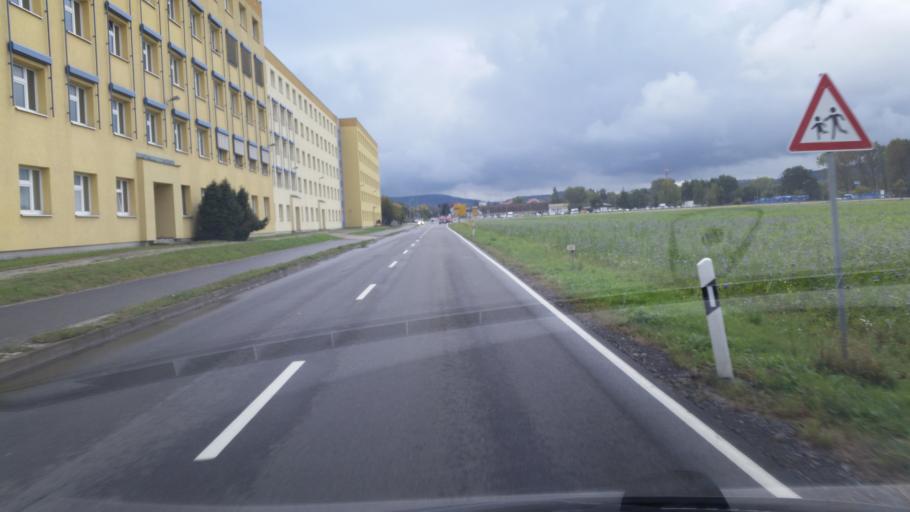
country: DE
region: Saxony
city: Kamenz
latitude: 51.2934
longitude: 14.1144
